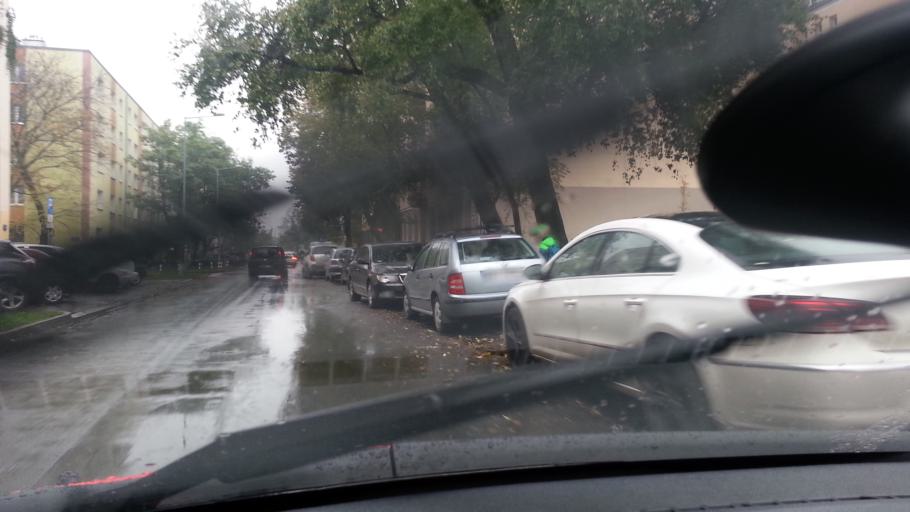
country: PL
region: Masovian Voivodeship
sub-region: Warszawa
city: Ochota
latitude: 52.2307
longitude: 20.9590
